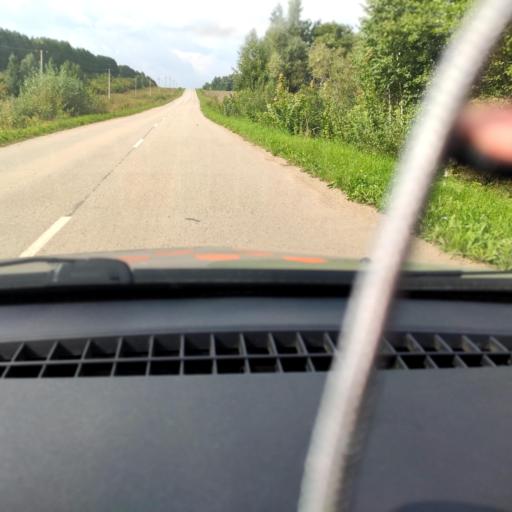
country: RU
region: Bashkortostan
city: Kudeyevskiy
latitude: 54.7402
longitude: 56.6016
